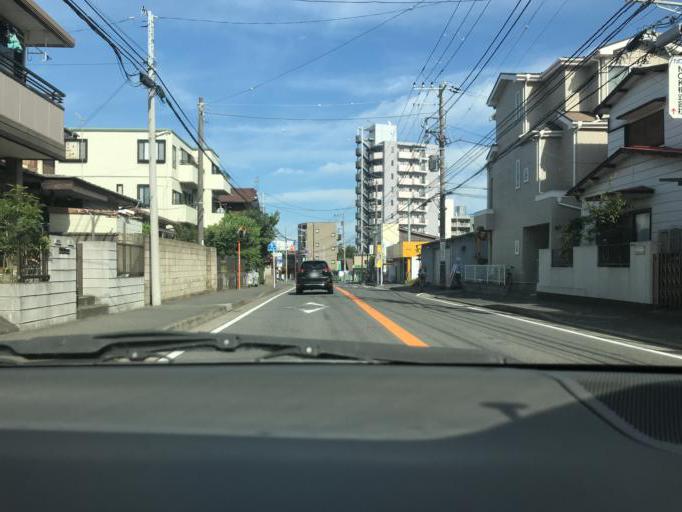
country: JP
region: Kanagawa
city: Fujisawa
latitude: 35.3412
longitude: 139.4606
